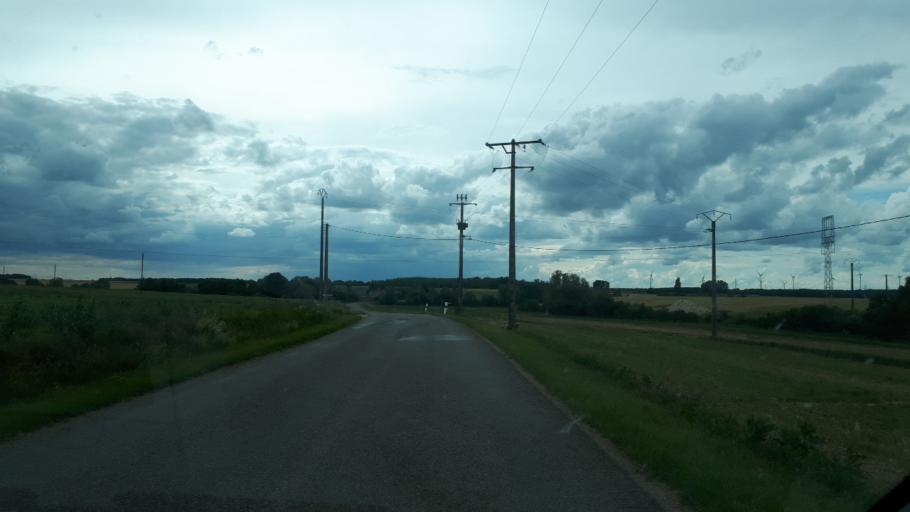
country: FR
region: Centre
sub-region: Departement de l'Indre
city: Reuilly
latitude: 47.0946
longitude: 2.0005
